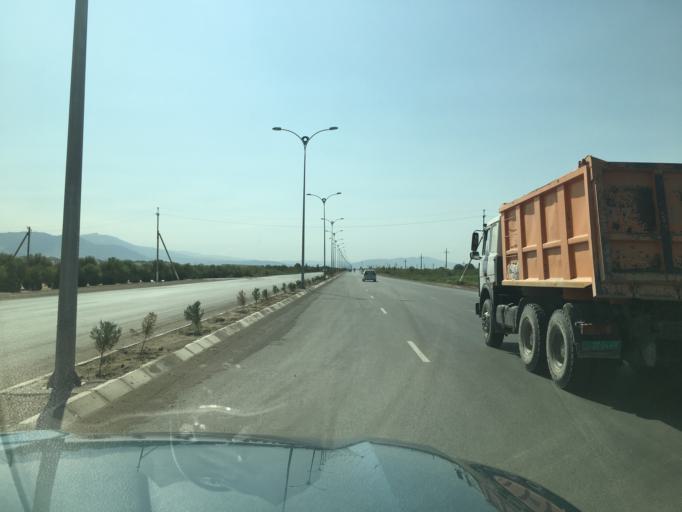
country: TM
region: Ahal
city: Abadan
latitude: 38.1028
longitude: 58.3054
